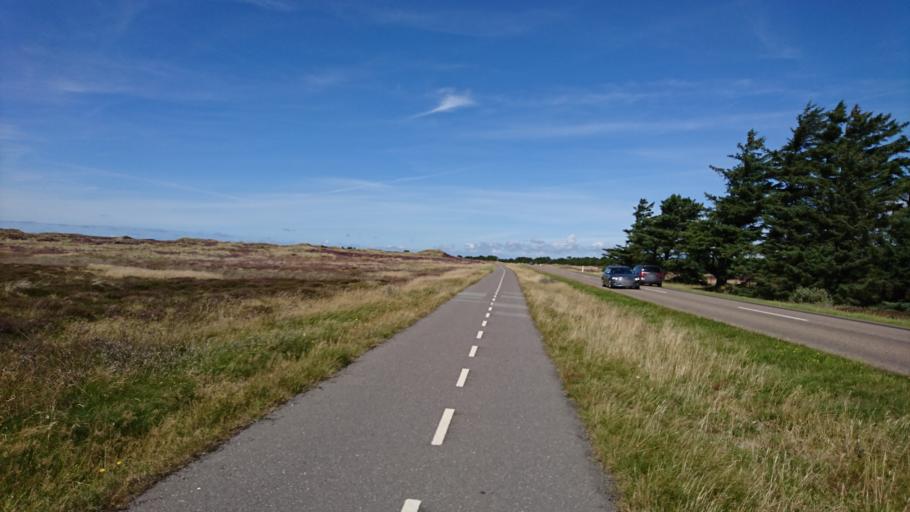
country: DK
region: South Denmark
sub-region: Fano Kommune
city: Nordby
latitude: 55.4089
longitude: 8.4134
